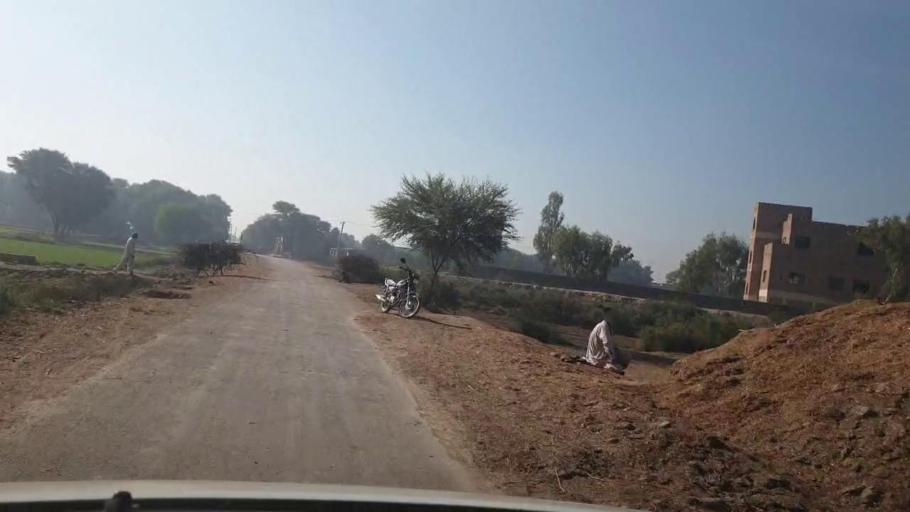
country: PK
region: Sindh
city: Dadu
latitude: 26.6504
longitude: 67.8221
